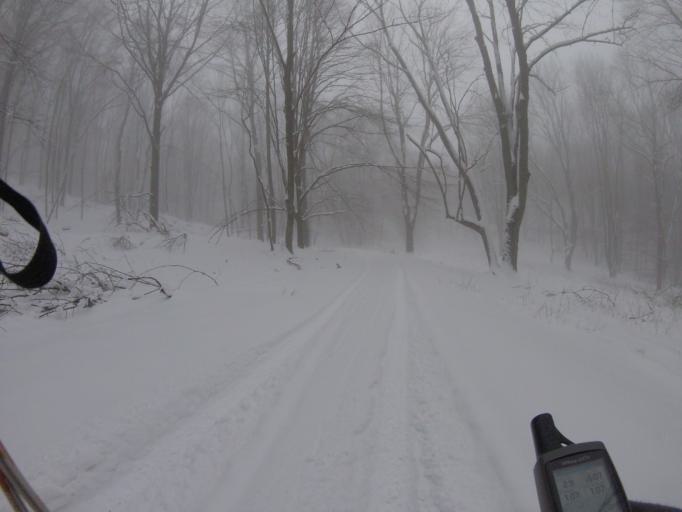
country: HU
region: Heves
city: Szilvasvarad
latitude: 48.0647
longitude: 20.4181
